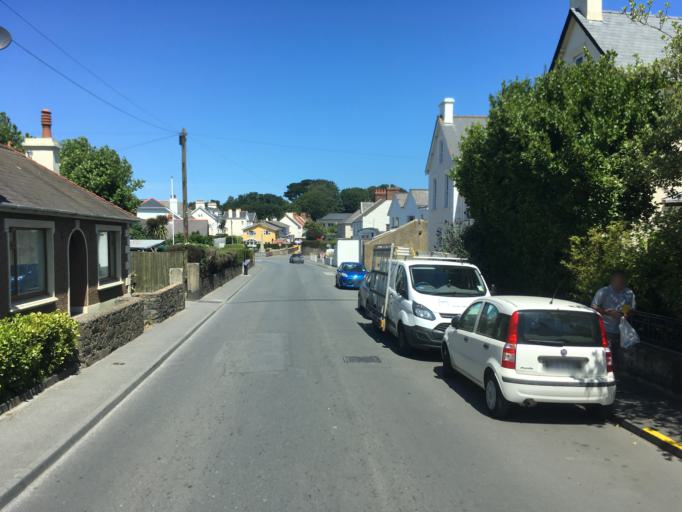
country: GG
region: St Peter Port
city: Saint Peter Port
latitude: 49.4857
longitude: -2.5190
